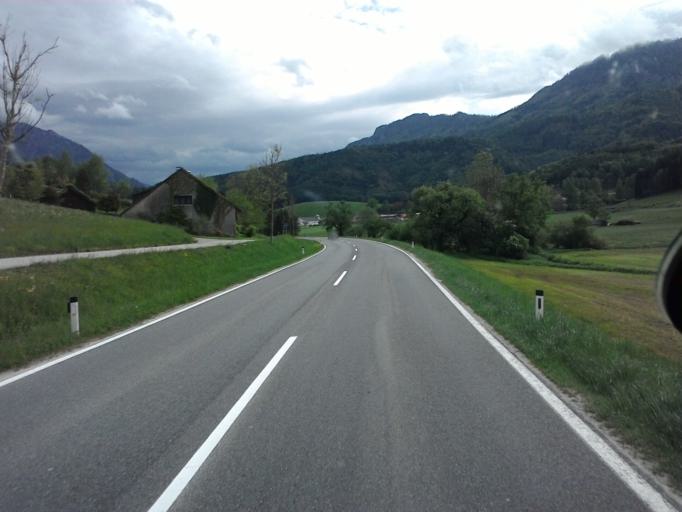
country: AT
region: Upper Austria
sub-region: Politischer Bezirk Kirchdorf an der Krems
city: Micheldorf in Oberoesterreich
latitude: 47.8568
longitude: 14.1500
